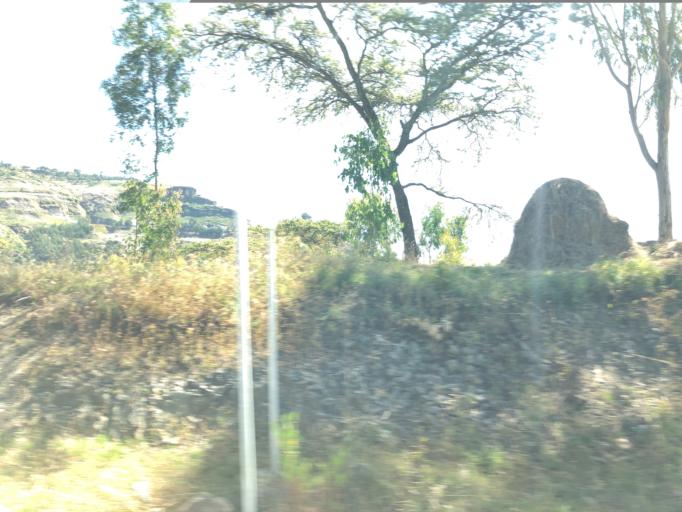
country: ET
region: Amhara
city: Lalibela
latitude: 11.8071
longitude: 38.5712
